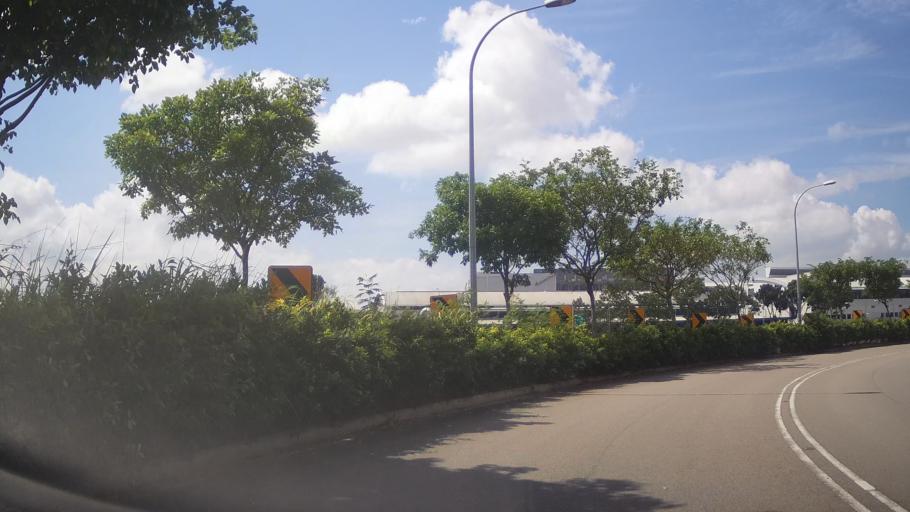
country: SG
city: Singapore
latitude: 1.3249
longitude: 103.7181
